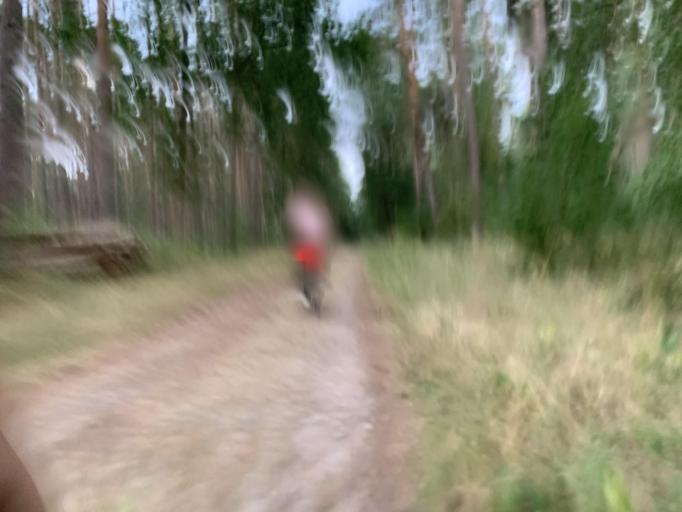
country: DE
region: Lower Saxony
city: Reinstorf
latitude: 53.2219
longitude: 10.6070
